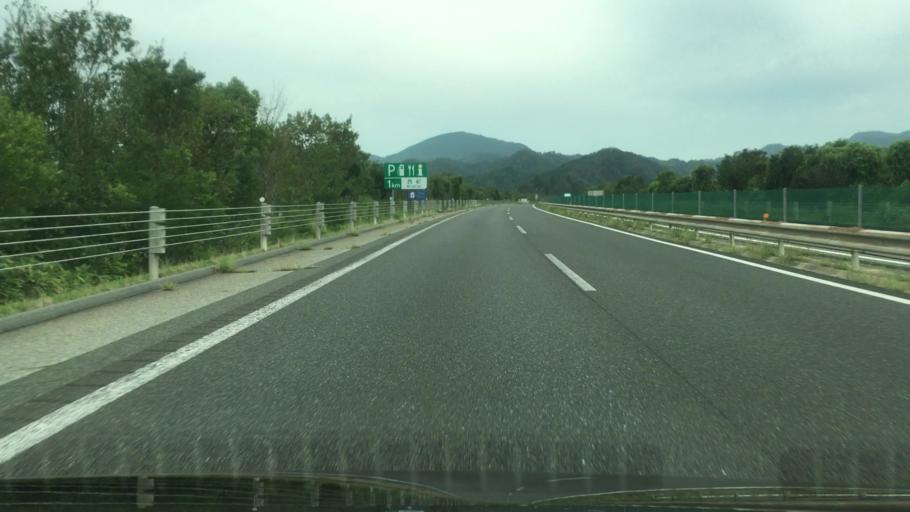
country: JP
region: Hyogo
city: Sasayama
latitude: 35.0794
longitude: 135.1687
